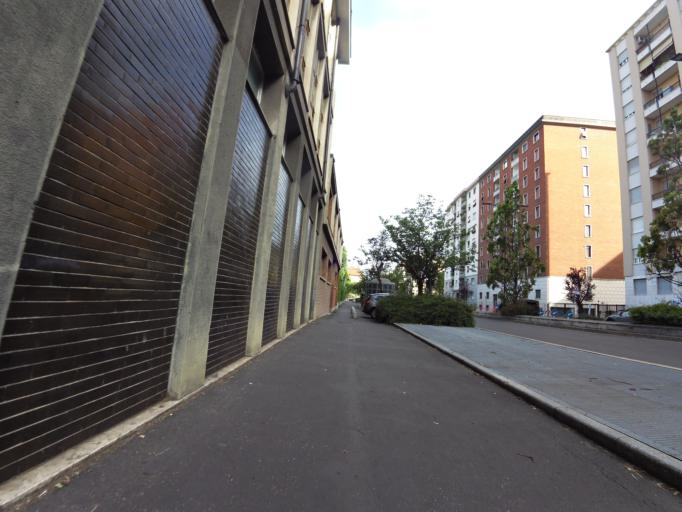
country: IT
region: Lombardy
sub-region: Citta metropolitana di Milano
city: Milano
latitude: 45.4731
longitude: 9.1615
